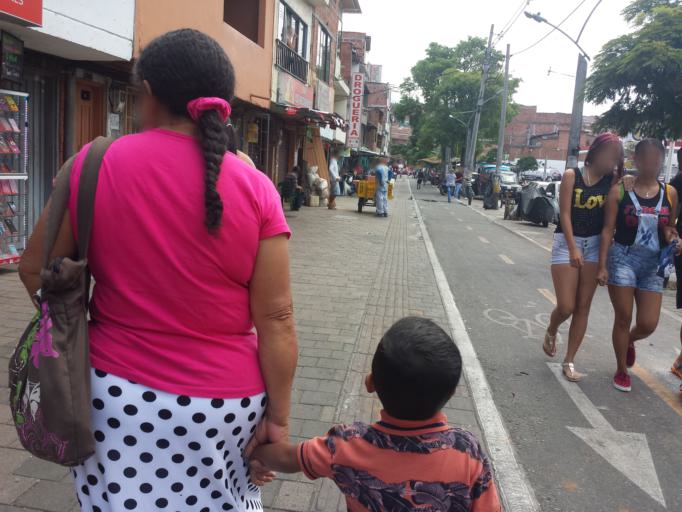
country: CO
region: Antioquia
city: Medellin
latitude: 6.2750
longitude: -75.5646
